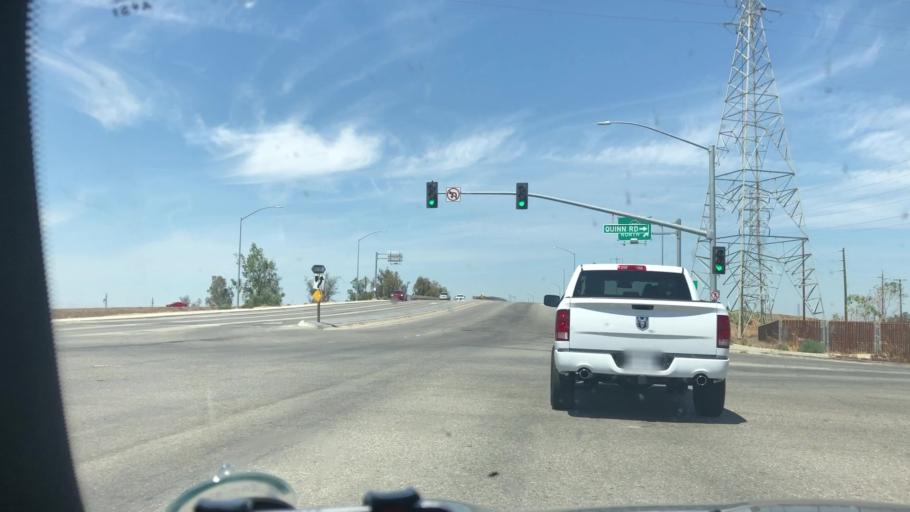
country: US
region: California
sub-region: Kern County
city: Greenacres
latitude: 35.4415
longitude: -119.0817
